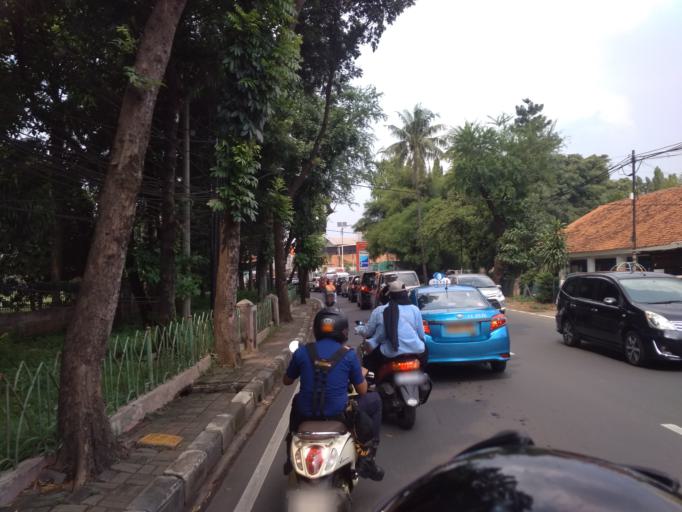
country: ID
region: Banten
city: South Tangerang
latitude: -6.2955
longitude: 106.7725
